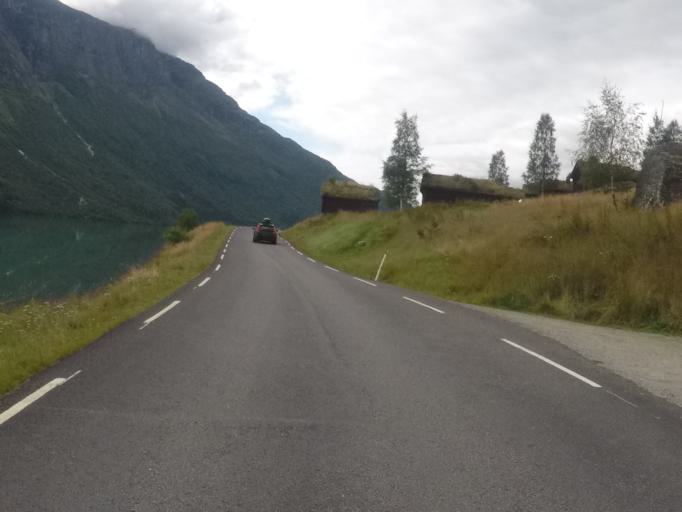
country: NO
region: Sogn og Fjordane
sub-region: Stryn
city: Stryn
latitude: 61.8411
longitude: 6.9436
